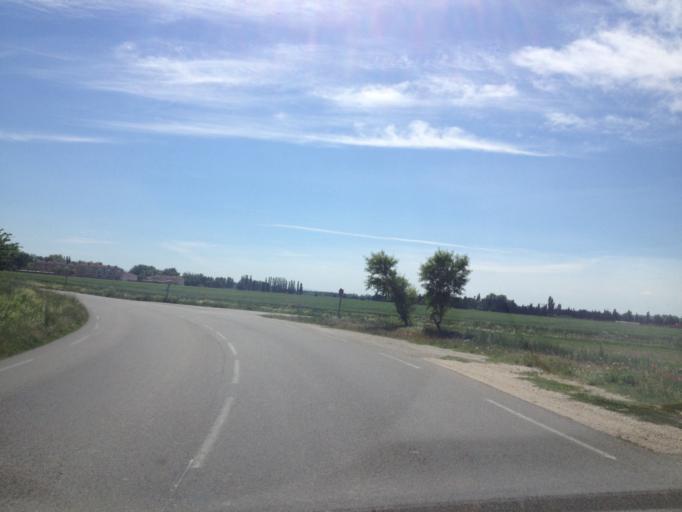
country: FR
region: Provence-Alpes-Cote d'Azur
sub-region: Departement du Vaucluse
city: Orange
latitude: 44.1442
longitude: 4.8385
